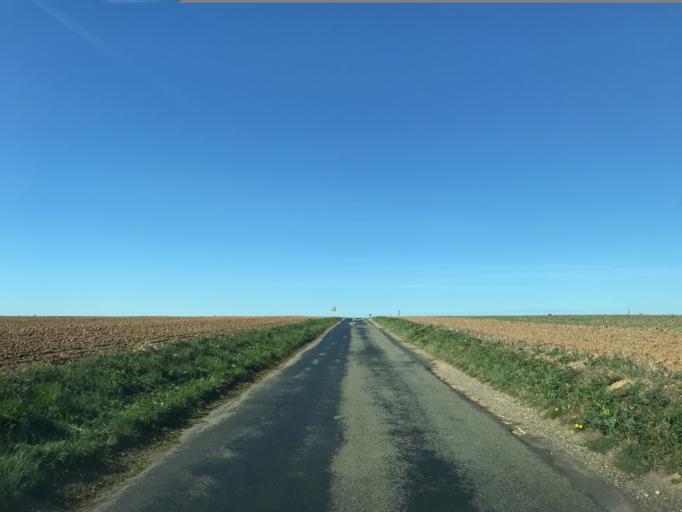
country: FR
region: Haute-Normandie
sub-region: Departement de l'Eure
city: Ande
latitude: 49.1817
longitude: 1.2472
